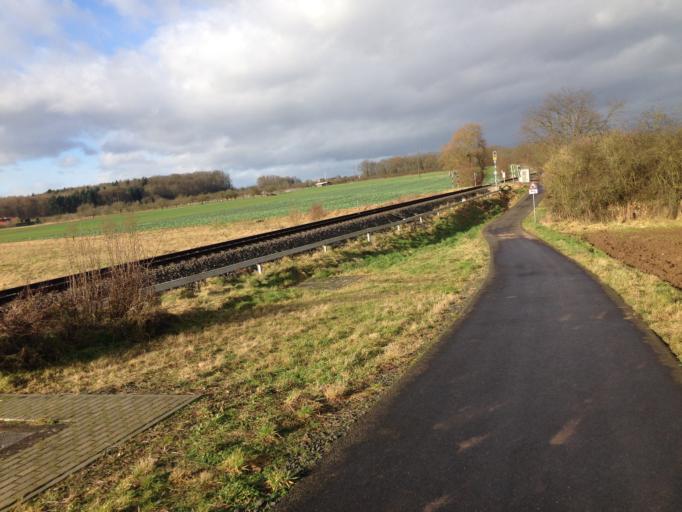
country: DE
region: Hesse
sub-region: Regierungsbezirk Giessen
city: Hungen
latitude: 50.4611
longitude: 8.9051
